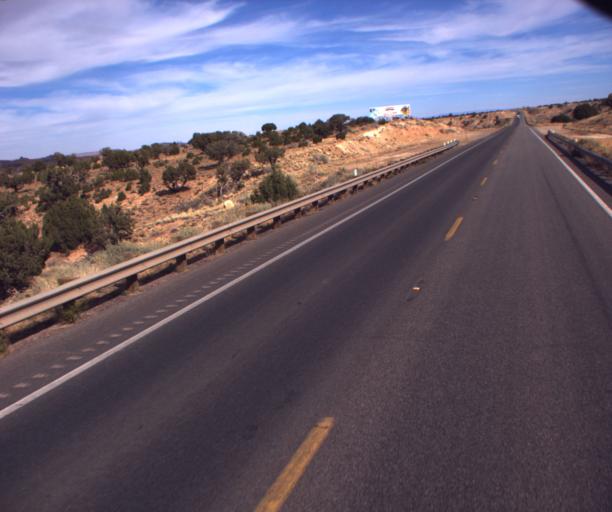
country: US
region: Arizona
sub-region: Navajo County
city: Kayenta
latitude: 36.6991
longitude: -110.3125
